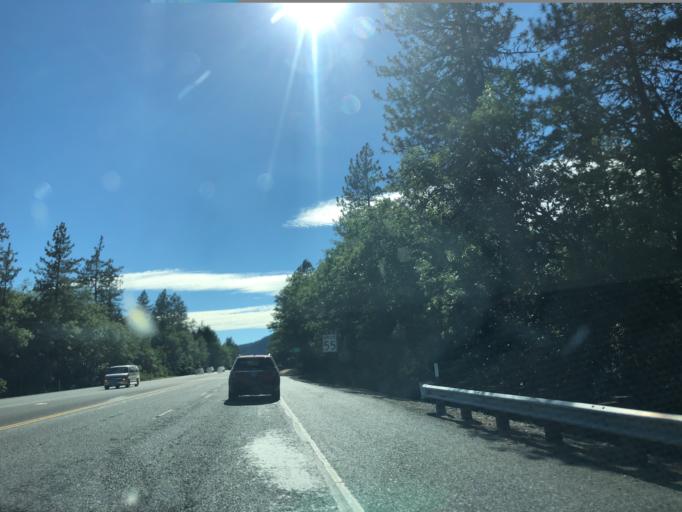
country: US
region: Oregon
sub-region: Josephine County
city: Redwood
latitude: 42.4124
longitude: -123.4137
